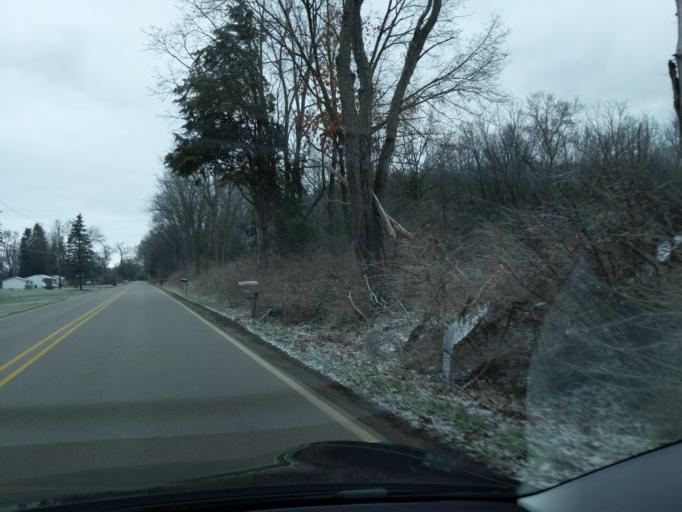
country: US
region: Michigan
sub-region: Jackson County
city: Spring Arbor
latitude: 42.2233
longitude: -84.5167
